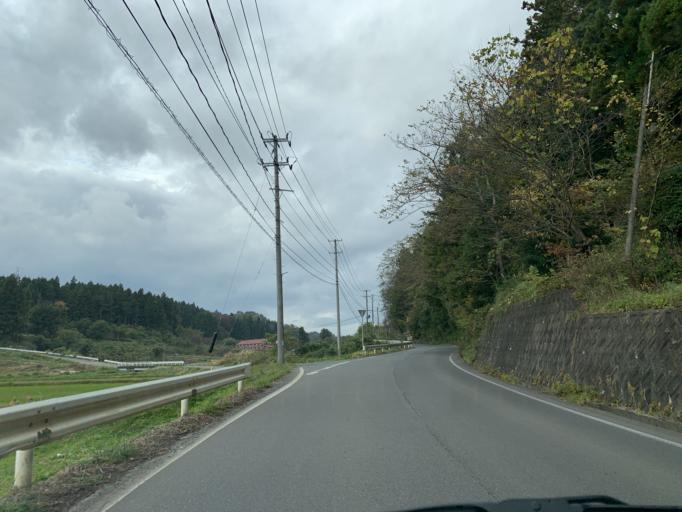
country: JP
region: Iwate
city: Mizusawa
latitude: 39.0434
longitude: 141.1174
